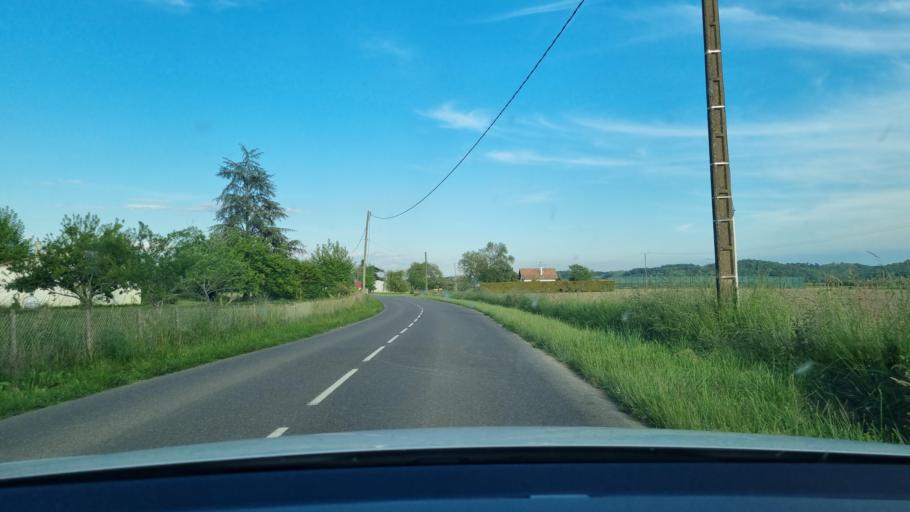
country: FR
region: Aquitaine
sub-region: Departement des Landes
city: Peyrehorade
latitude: 43.5417
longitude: -1.1368
